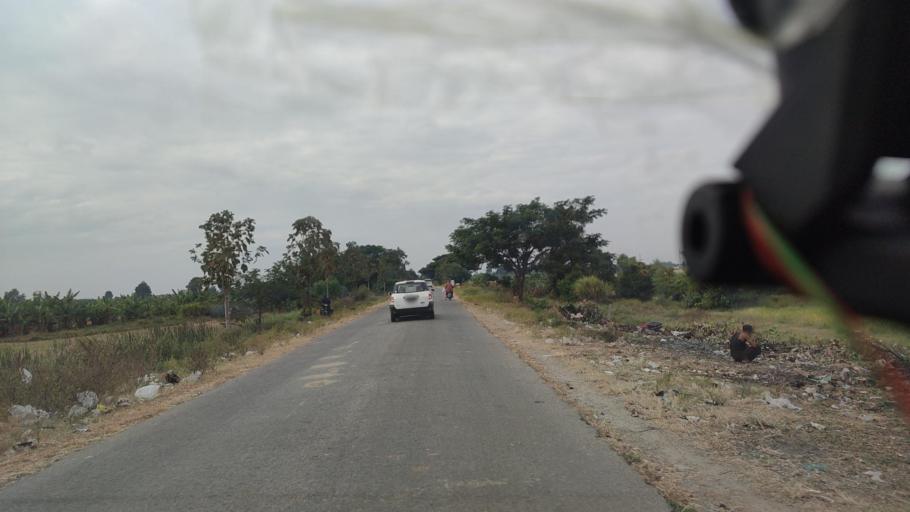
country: MM
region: Mandalay
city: Pyinmana
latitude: 19.7572
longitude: 96.3034
